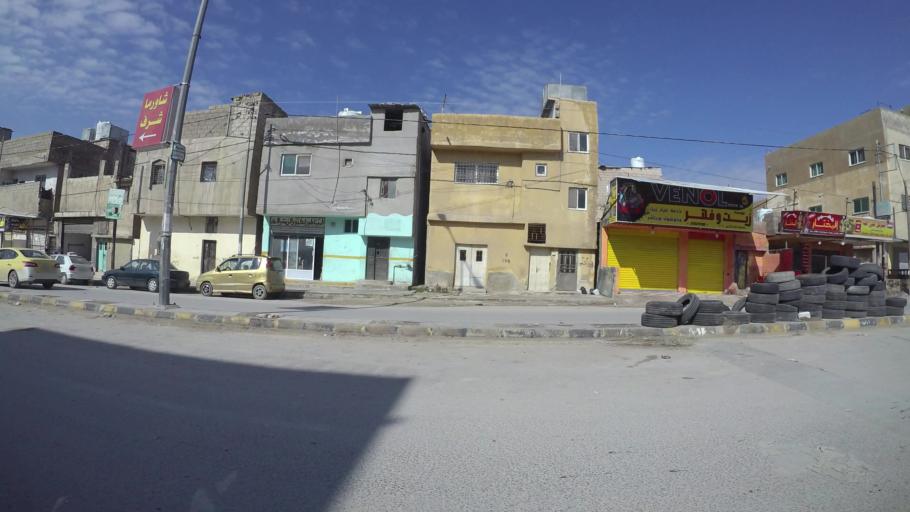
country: JO
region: Amman
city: Al Jubayhah
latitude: 32.0669
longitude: 35.8424
